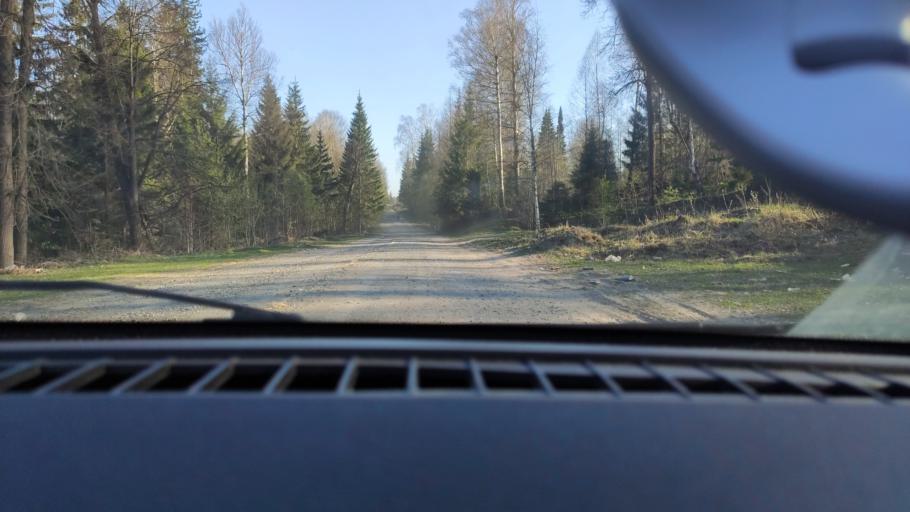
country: RU
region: Perm
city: Polazna
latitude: 58.1354
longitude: 56.4575
